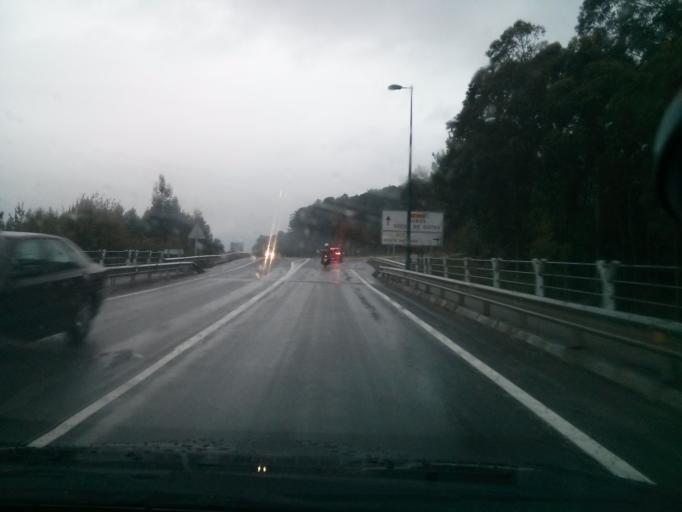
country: ES
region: Galicia
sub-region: Provincia da Coruna
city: Noia
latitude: 42.8172
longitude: -8.8870
